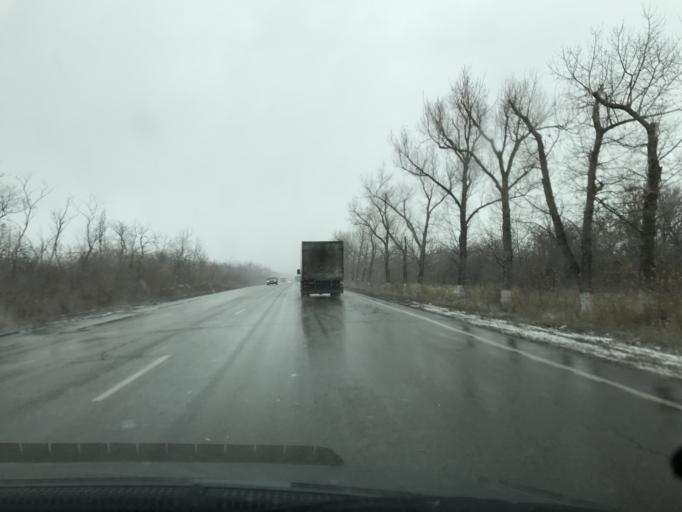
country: RU
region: Rostov
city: Bataysk
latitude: 47.0591
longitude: 39.8198
